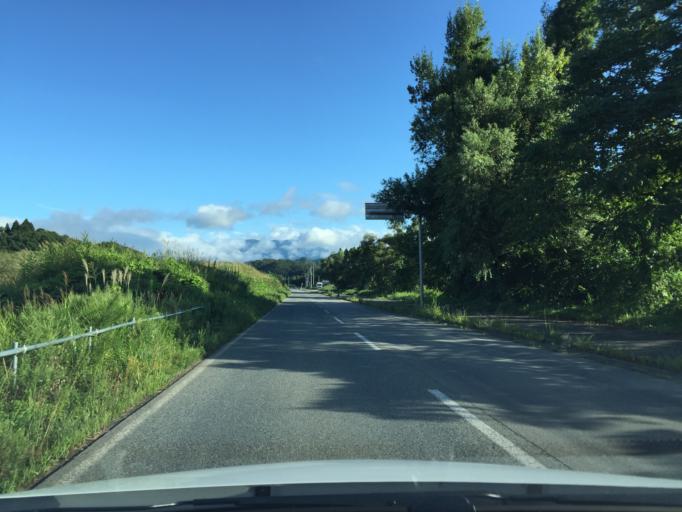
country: JP
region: Yamagata
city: Yonezawa
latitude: 37.9211
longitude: 140.1590
